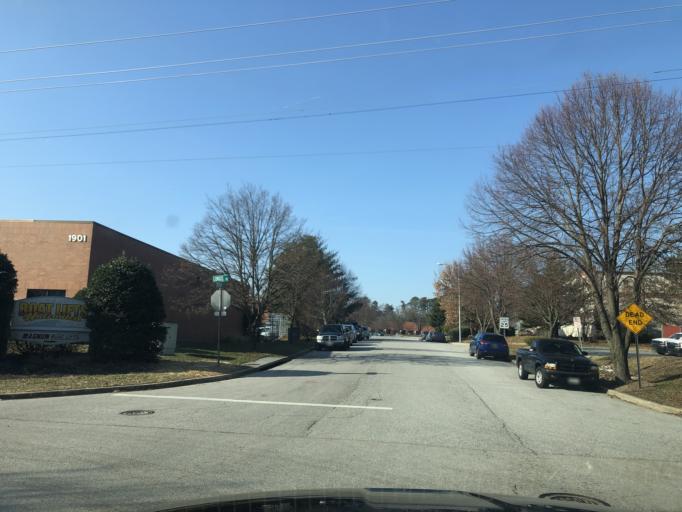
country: US
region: Maryland
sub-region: Anne Arundel County
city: Odenton
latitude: 39.0972
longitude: -76.6988
